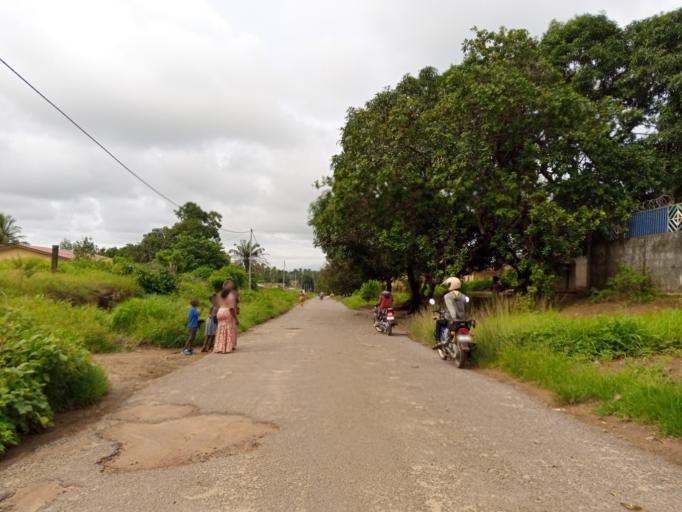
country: SL
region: Northern Province
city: Masoyila
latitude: 8.6008
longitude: -13.1961
